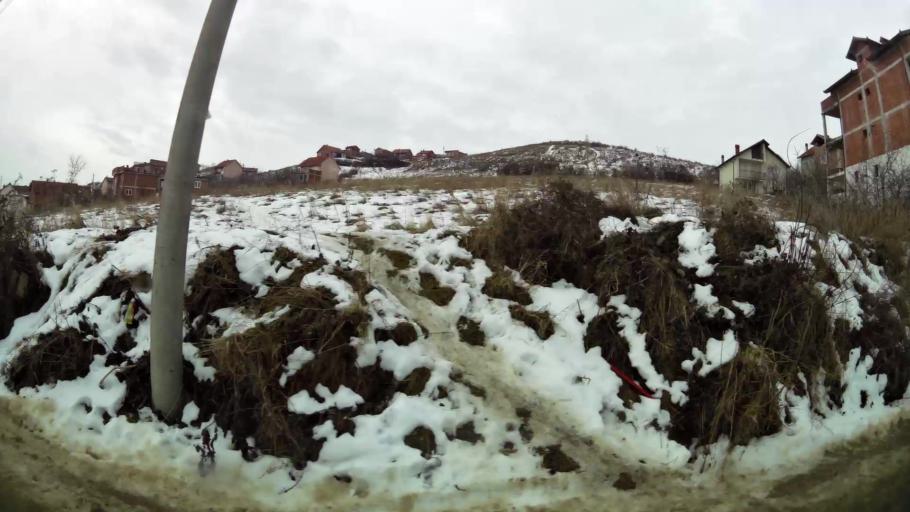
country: XK
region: Pristina
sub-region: Komuna e Prishtines
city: Pristina
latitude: 42.6875
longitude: 21.1728
